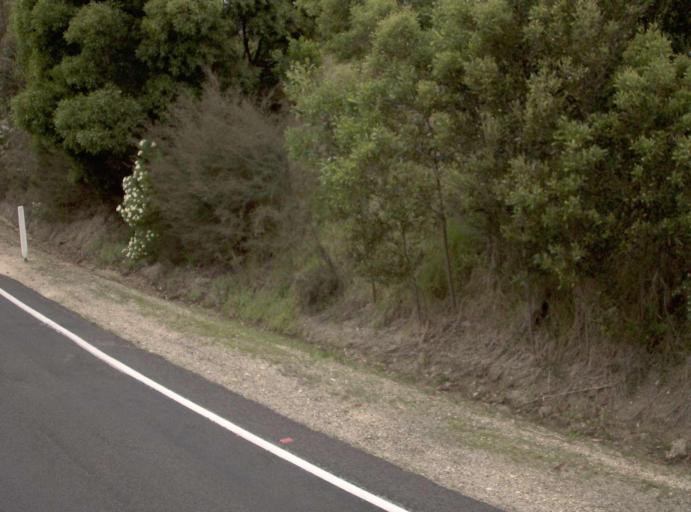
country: AU
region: New South Wales
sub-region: Bombala
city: Bombala
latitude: -37.4740
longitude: 149.1765
